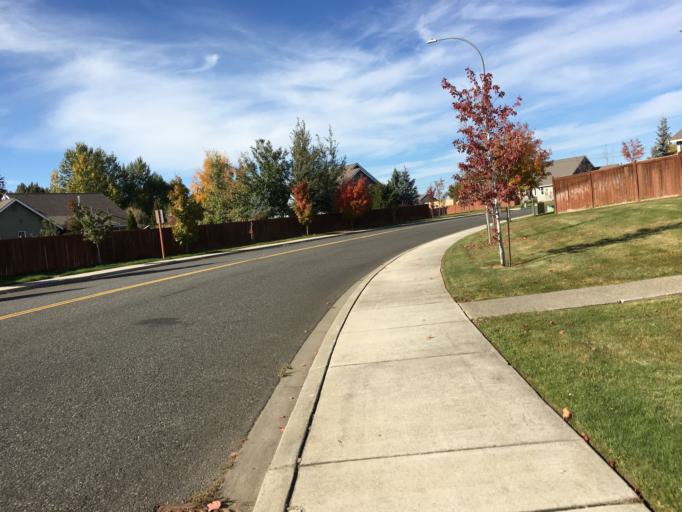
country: US
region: Washington
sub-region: Kittitas County
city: Ellensburg
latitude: 47.0205
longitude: -120.5328
